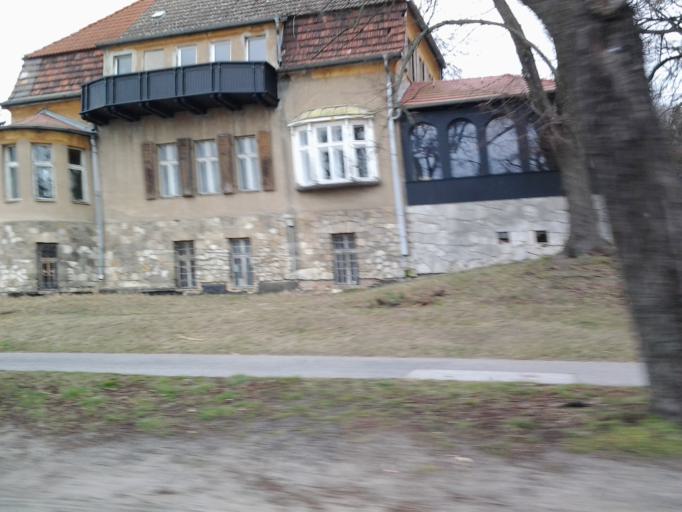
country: DE
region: Brandenburg
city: Werder
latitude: 52.4035
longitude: 12.9743
